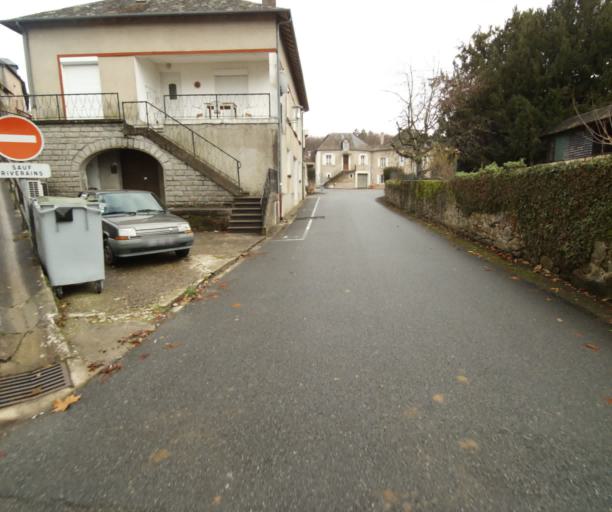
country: FR
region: Limousin
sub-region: Departement de la Correze
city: Saint-Mexant
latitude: 45.2737
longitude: 1.6343
